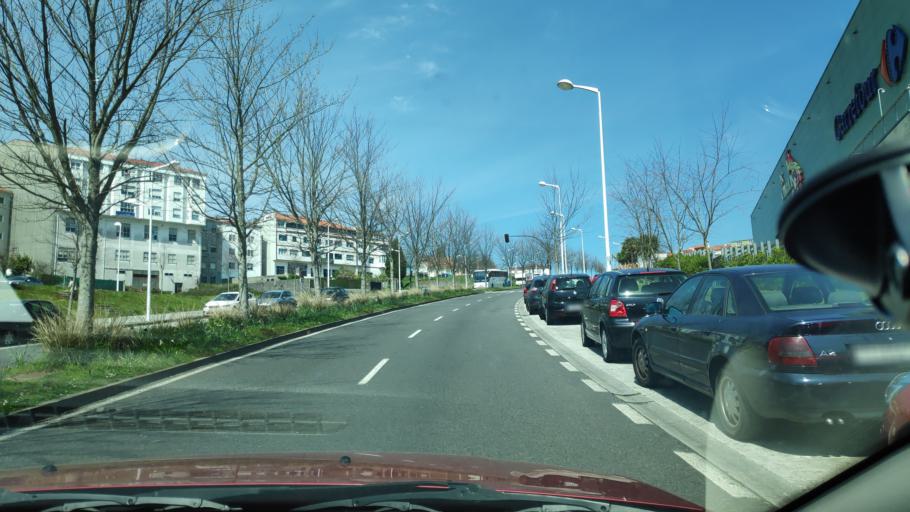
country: ES
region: Galicia
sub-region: Provincia da Coruna
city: Santiago de Compostela
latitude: 42.8893
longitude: -8.5279
